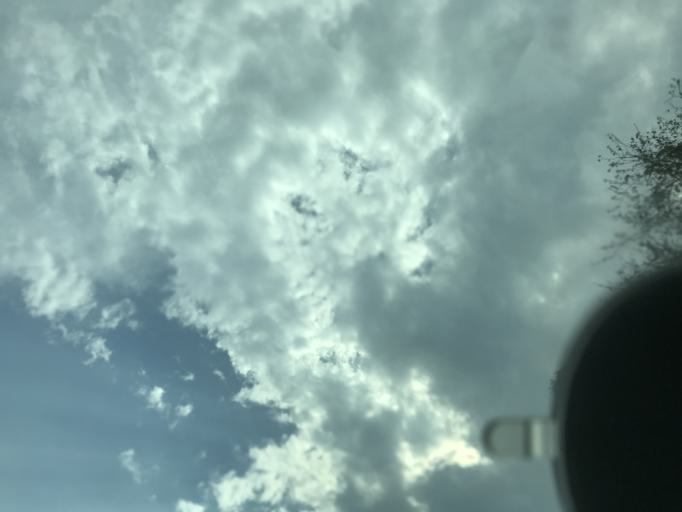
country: GT
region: Zacapa
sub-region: Municipio de Zacapa
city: Gualan
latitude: 15.1825
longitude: -89.2967
